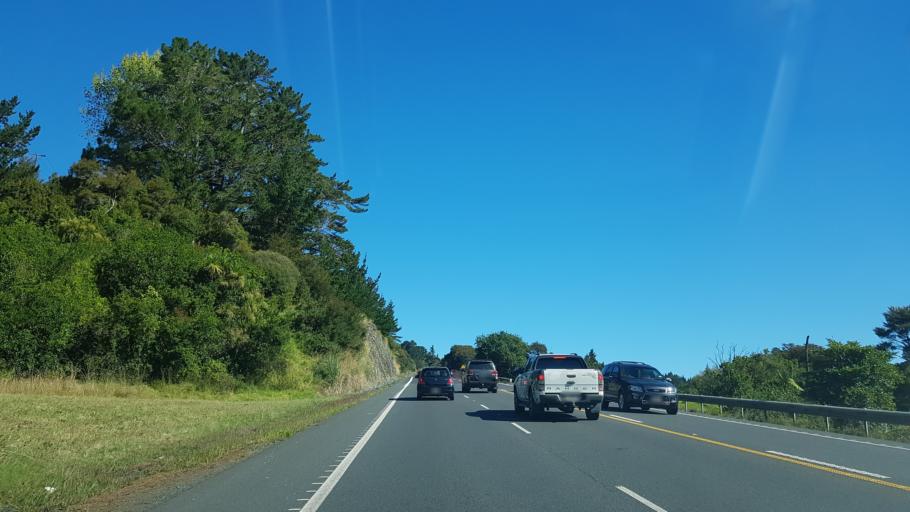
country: NZ
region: Auckland
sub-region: Auckland
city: Warkworth
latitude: -36.4545
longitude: 174.6526
